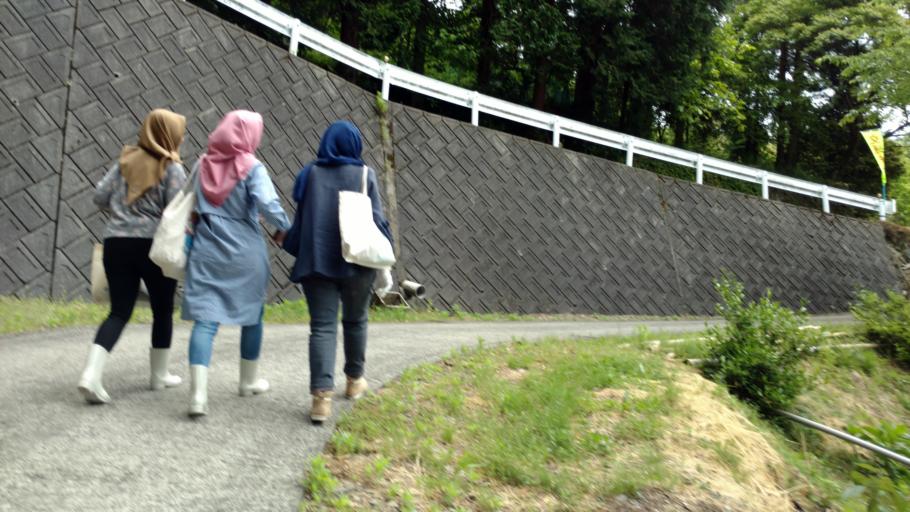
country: JP
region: Ehime
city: Saijo
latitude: 33.8666
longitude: 133.1989
